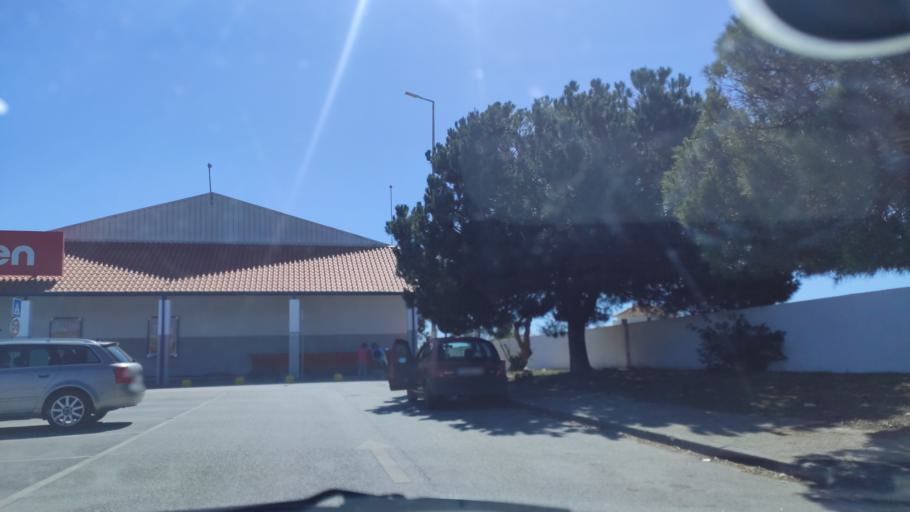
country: PT
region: Faro
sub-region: Olhao
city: Olhao
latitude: 37.0292
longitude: -7.8564
